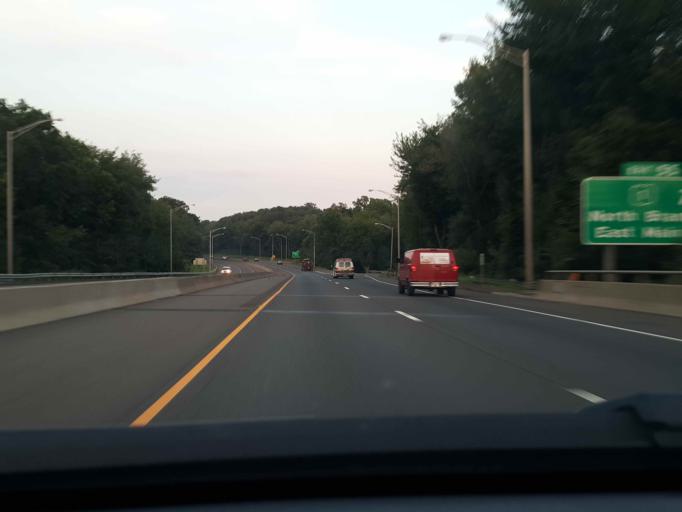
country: US
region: Connecticut
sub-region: New Haven County
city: Branford
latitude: 41.2941
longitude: -72.7837
